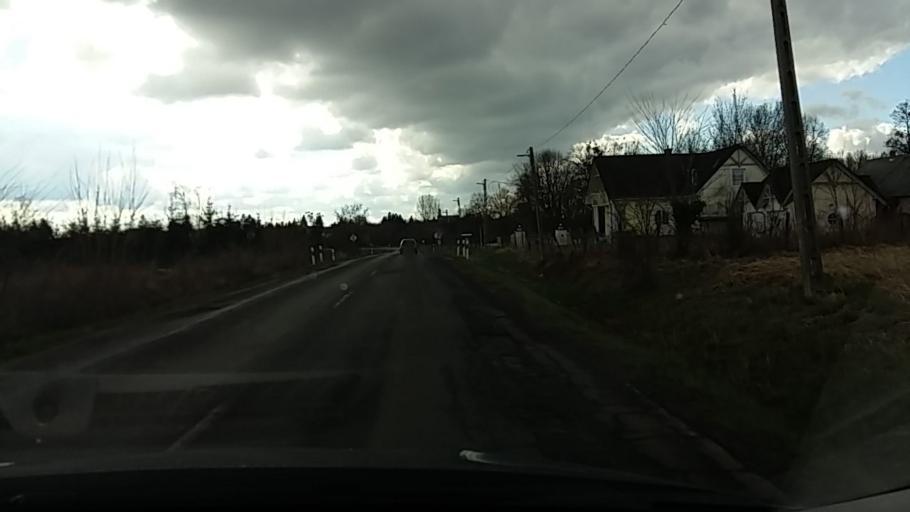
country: HU
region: Somogy
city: Bohonye
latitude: 46.4155
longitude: 17.3832
